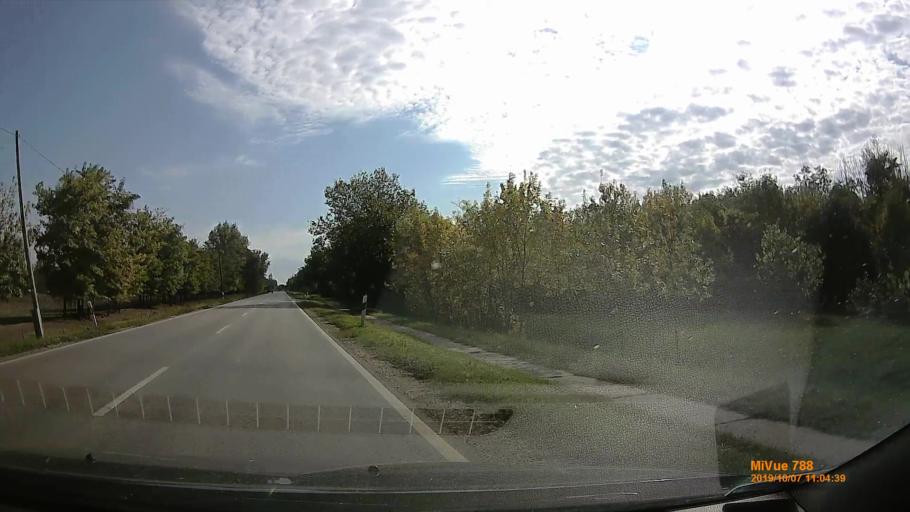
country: HU
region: Bekes
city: Kondoros
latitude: 46.7534
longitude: 20.8224
